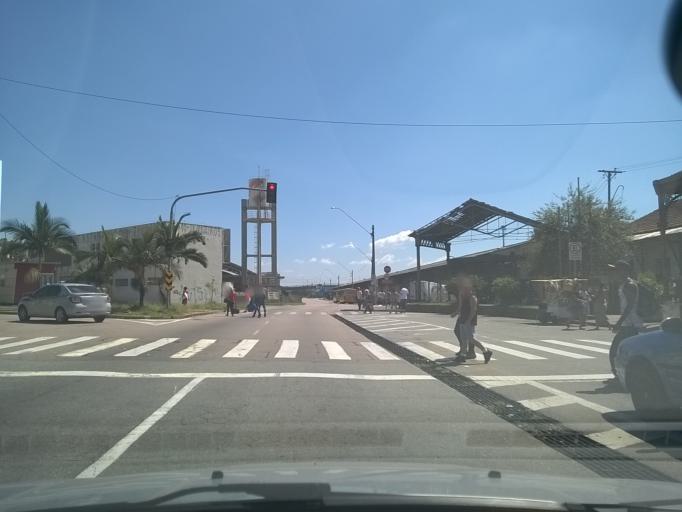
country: BR
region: Sao Paulo
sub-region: Jundiai
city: Jundiai
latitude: -23.1952
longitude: -46.8727
